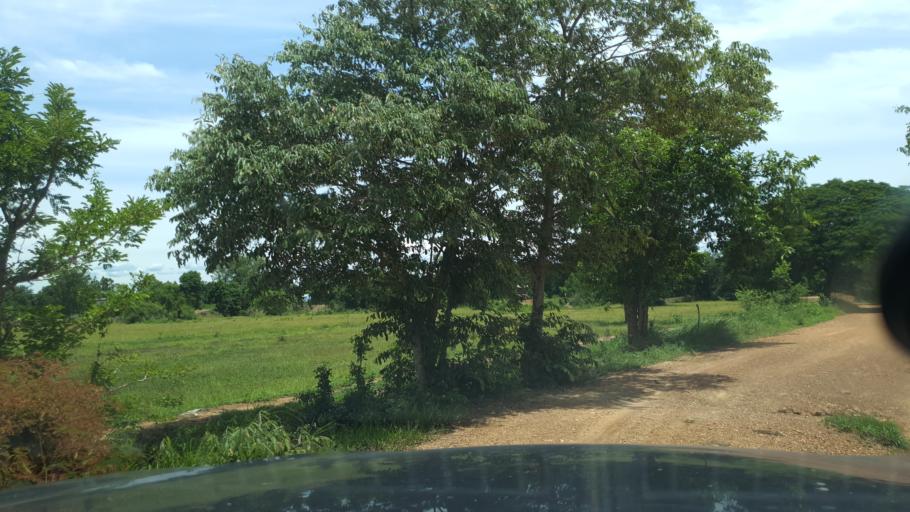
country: TH
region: Sukhothai
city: Ban Na
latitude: 17.0832
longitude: 99.6901
